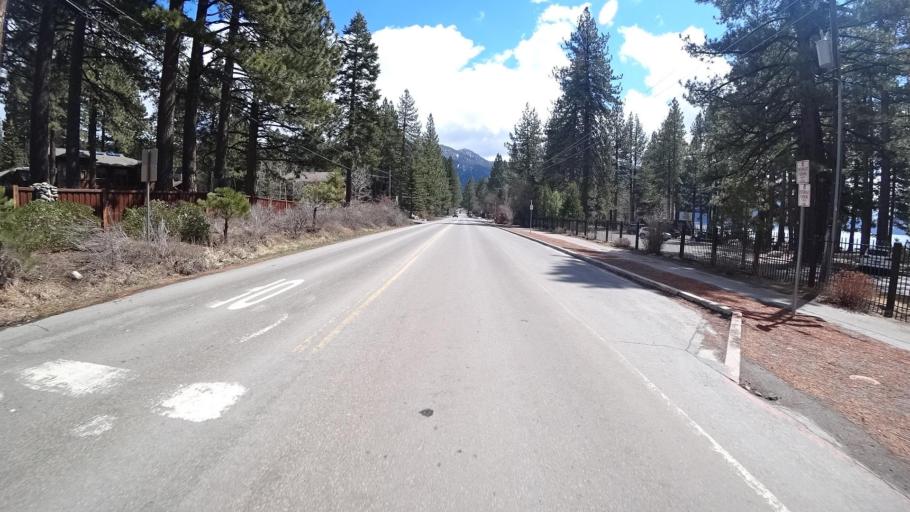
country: US
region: Nevada
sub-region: Washoe County
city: Incline Village
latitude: 39.2409
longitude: -119.9489
